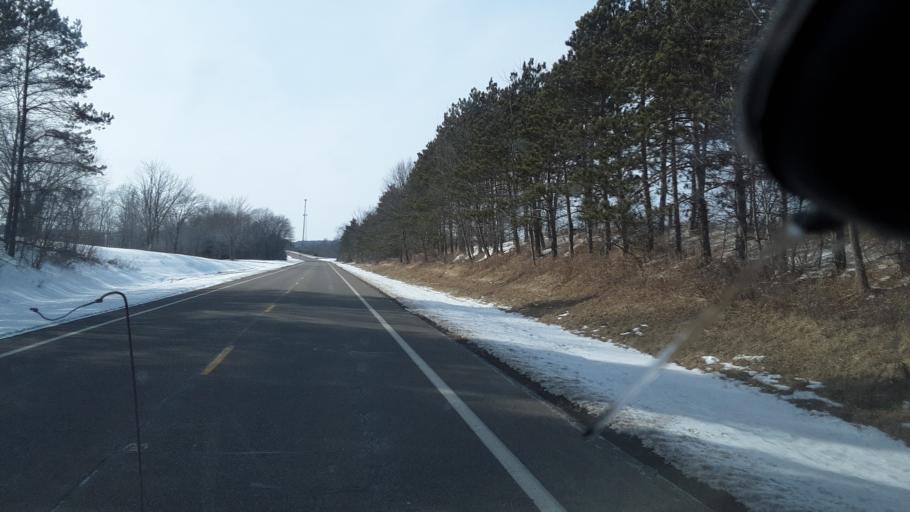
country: US
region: Ohio
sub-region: Stark County
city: Alliance
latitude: 41.0320
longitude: -81.1590
